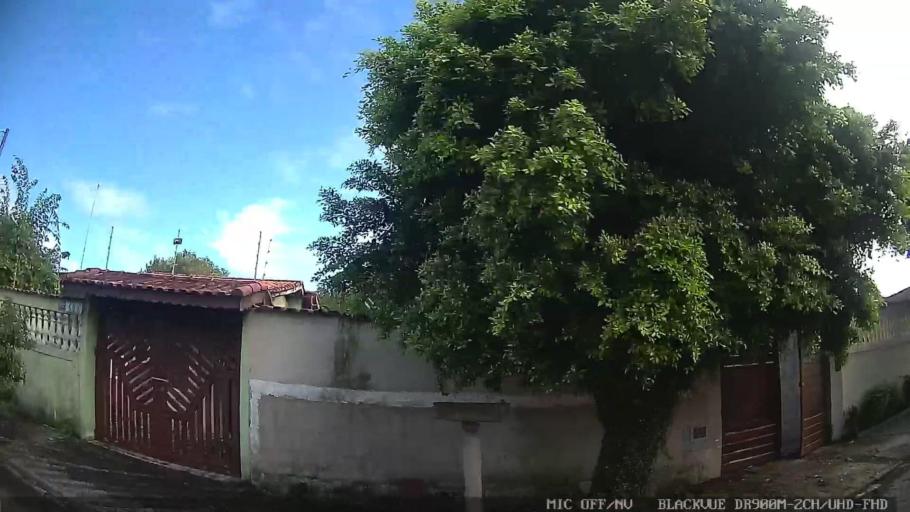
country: BR
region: Sao Paulo
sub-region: Itanhaem
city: Itanhaem
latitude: -24.2438
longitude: -46.8931
